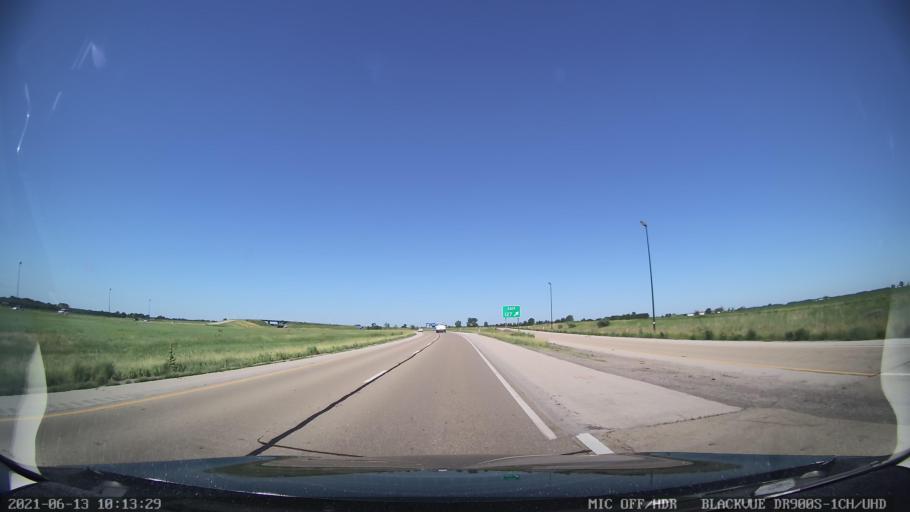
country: US
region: Illinois
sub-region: Logan County
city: Lincoln
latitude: 40.1815
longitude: -89.4071
